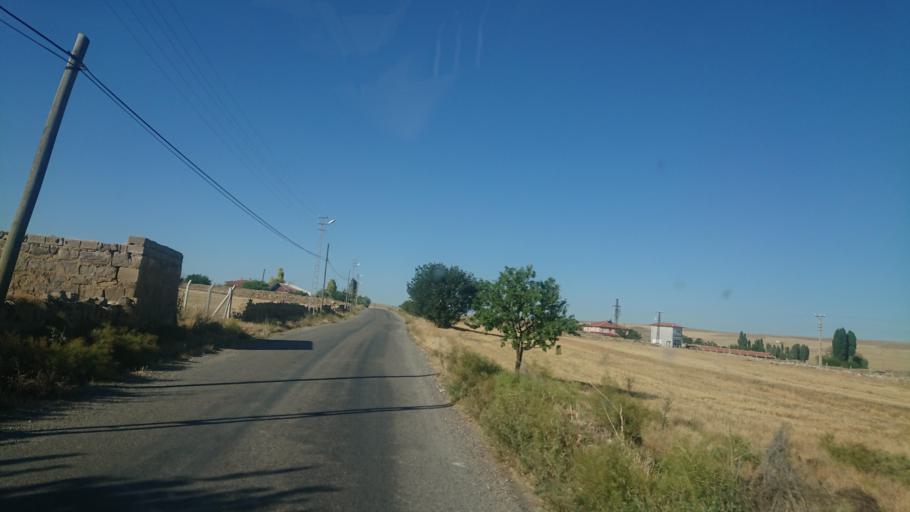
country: TR
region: Aksaray
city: Agacoren
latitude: 38.7716
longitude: 33.7053
